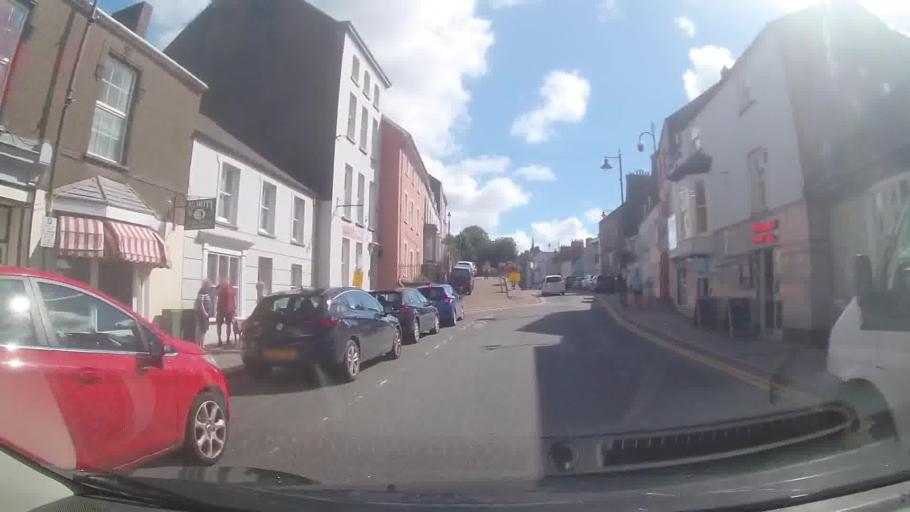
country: GB
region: Wales
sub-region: Pembrokeshire
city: Pembroke
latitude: 51.6754
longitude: -4.9153
